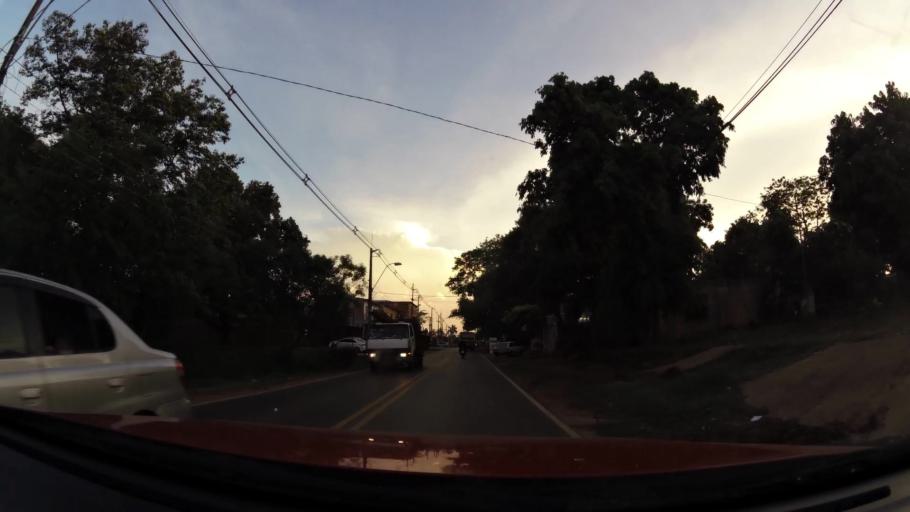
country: PY
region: Central
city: San Lorenzo
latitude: -25.3725
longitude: -57.4919
